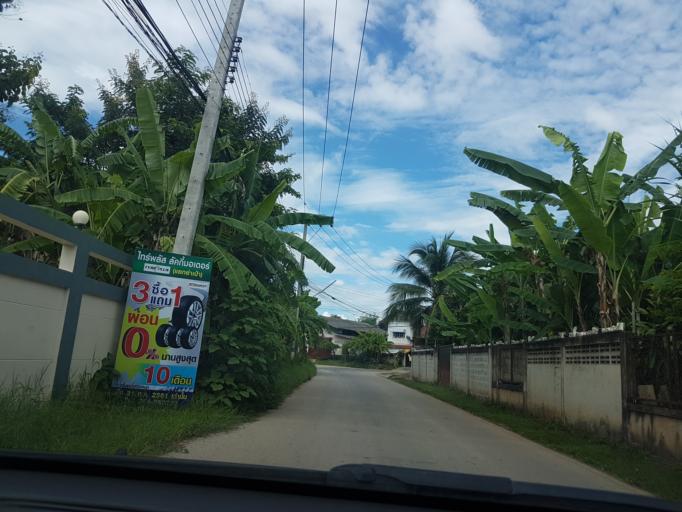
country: TH
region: Lampang
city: Ko Kha
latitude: 18.2351
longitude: 99.4242
